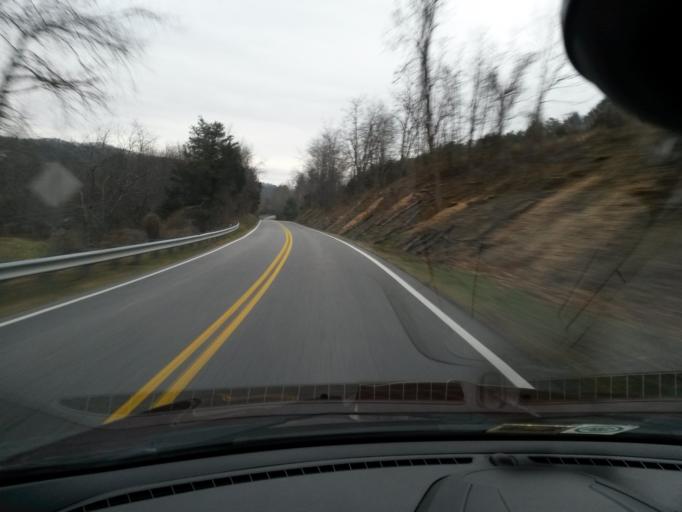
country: US
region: Virginia
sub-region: Bath County
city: Warm Springs
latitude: 38.0371
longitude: -79.6591
